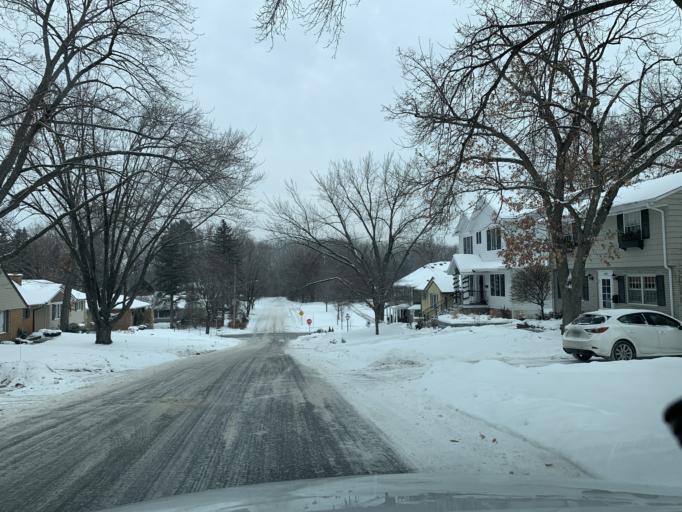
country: US
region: Minnesota
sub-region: Hennepin County
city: Edina
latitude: 44.9161
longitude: -93.3581
